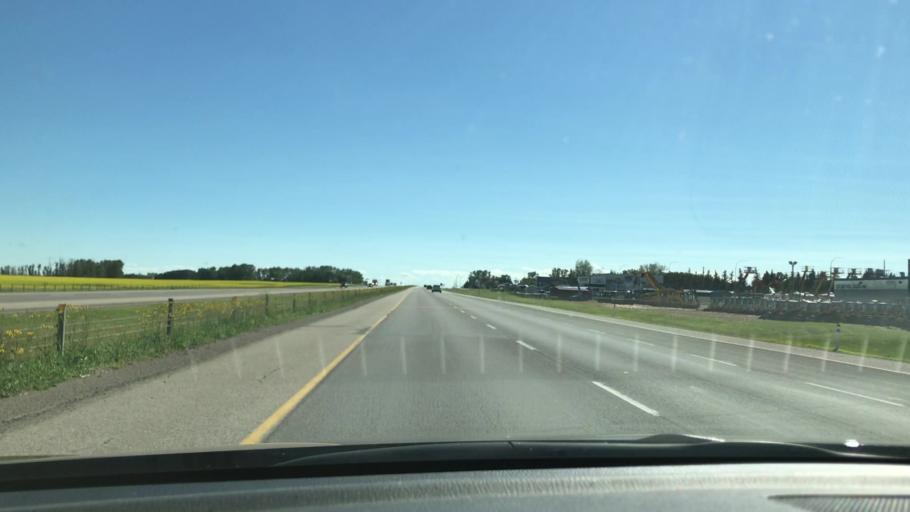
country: CA
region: Alberta
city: Penhold
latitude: 52.0203
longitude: -113.9390
